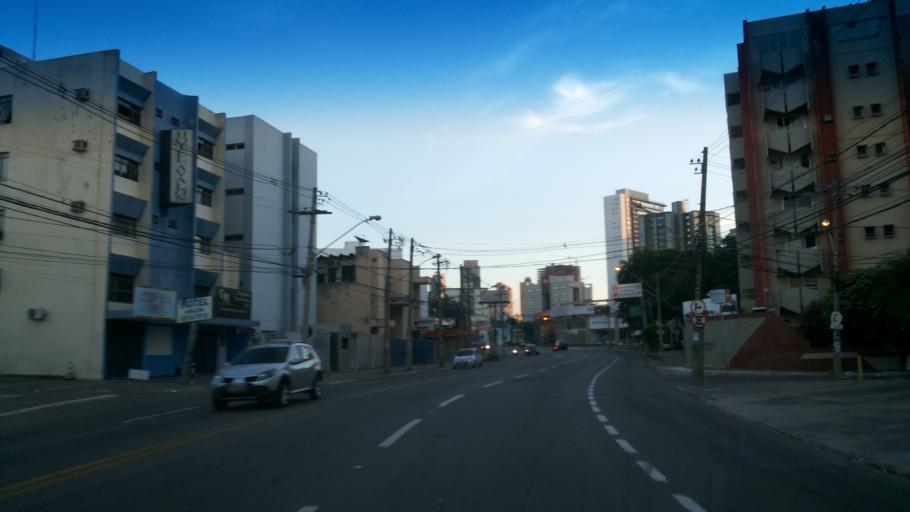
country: BR
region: Goias
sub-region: Goiania
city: Goiania
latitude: -16.6880
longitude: -49.2600
